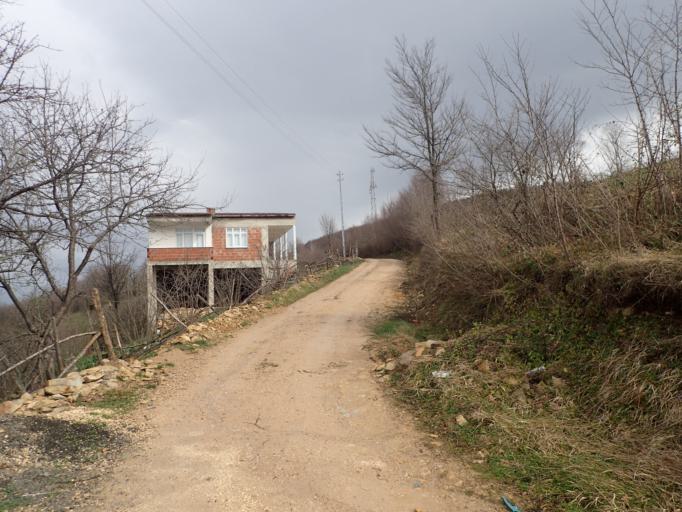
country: TR
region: Ordu
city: Kumru
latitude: 40.9468
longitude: 37.2538
